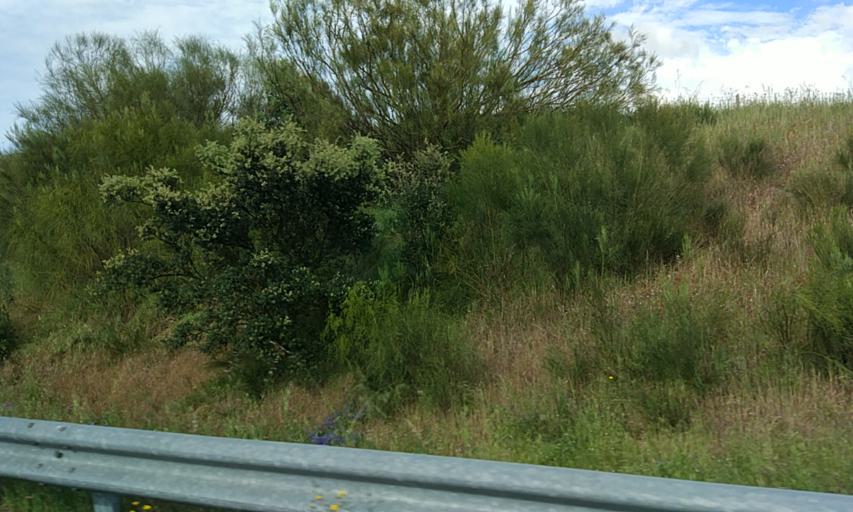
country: PT
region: Evora
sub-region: Evora
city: Evora
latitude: 38.6453
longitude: -7.8561
